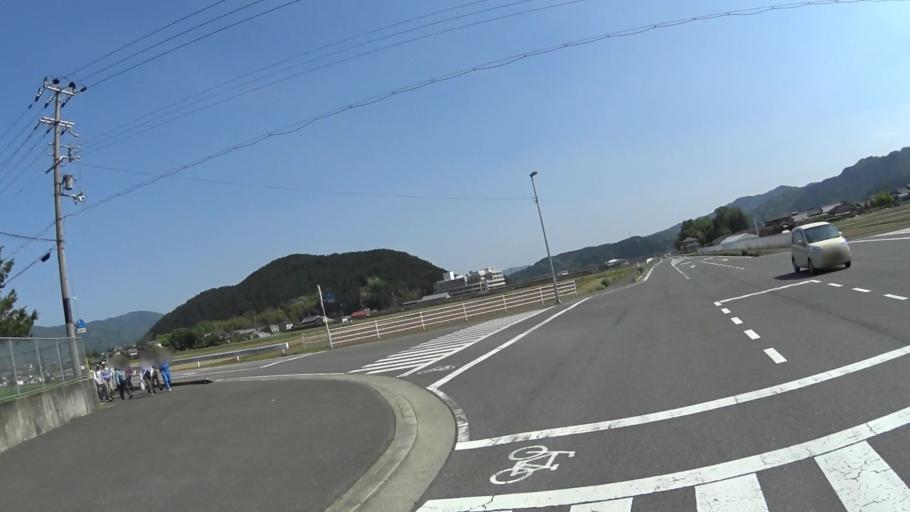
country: JP
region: Kyoto
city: Kameoka
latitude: 35.0847
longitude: 135.5376
